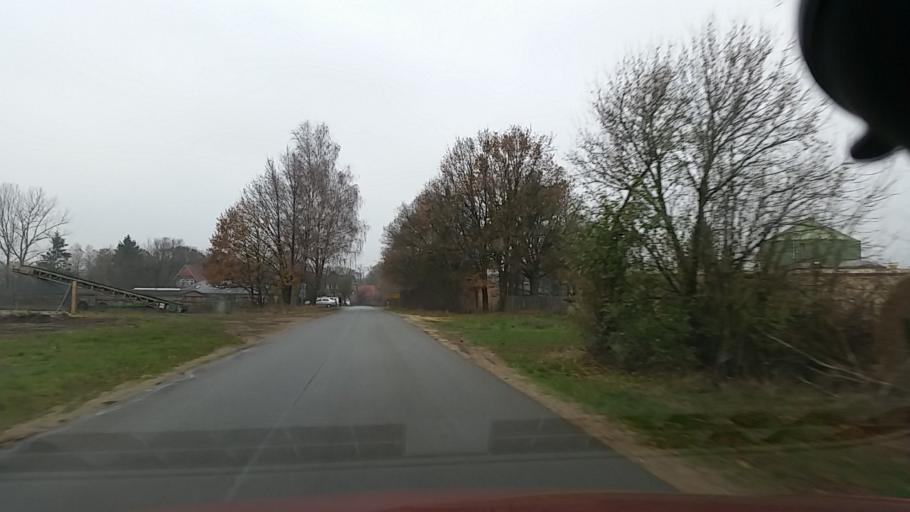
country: DE
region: Lower Saxony
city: Obernholz
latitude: 52.8053
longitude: 10.5502
